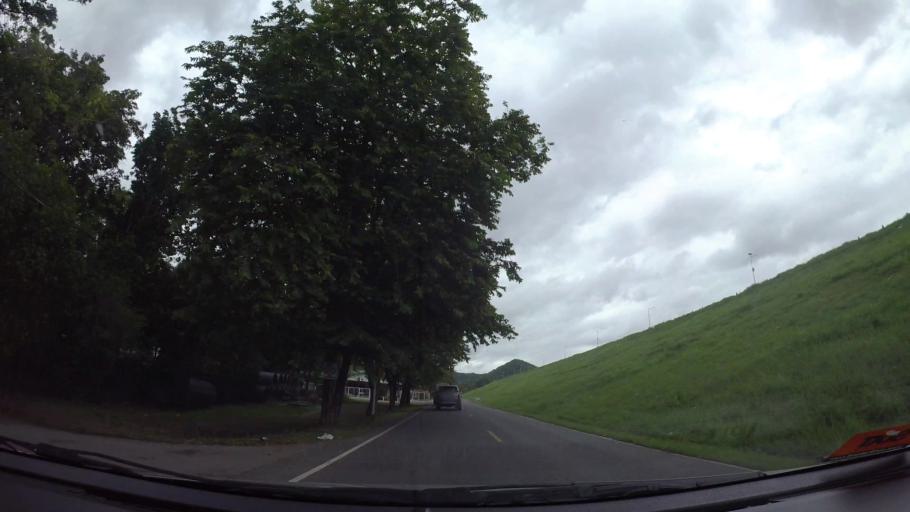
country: TH
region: Chon Buri
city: Si Racha
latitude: 13.2146
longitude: 100.9625
